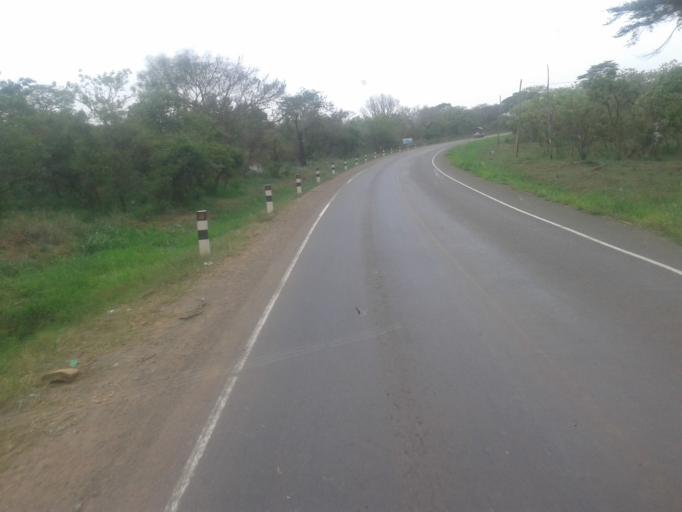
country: UG
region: Northern Region
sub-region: Oyam District
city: Oyam
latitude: 2.2493
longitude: 32.2358
